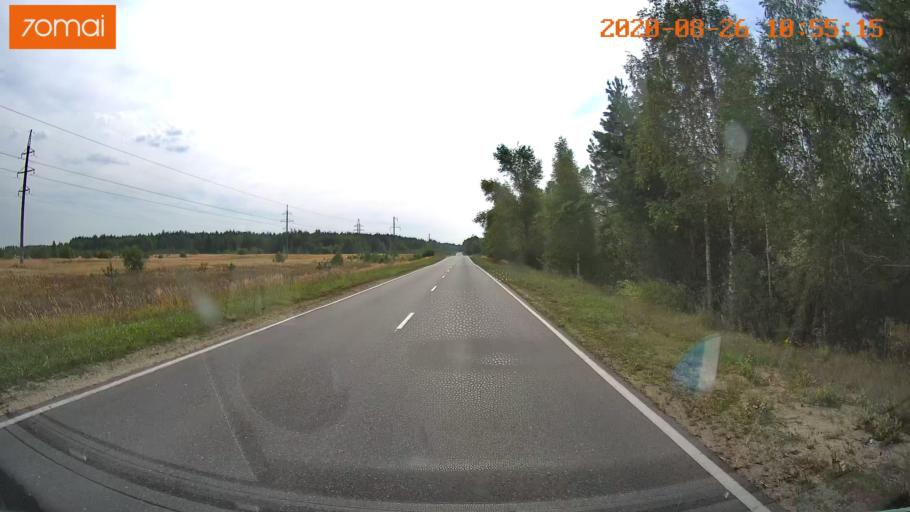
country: RU
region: Rjazan
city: Izhevskoye
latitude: 54.6185
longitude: 41.1749
